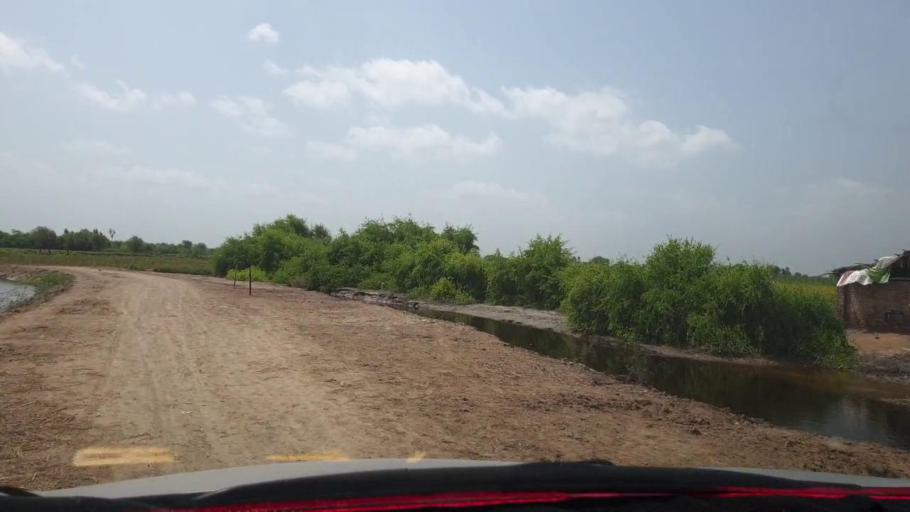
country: PK
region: Sindh
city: Talhar
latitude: 24.9006
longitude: 68.8468
